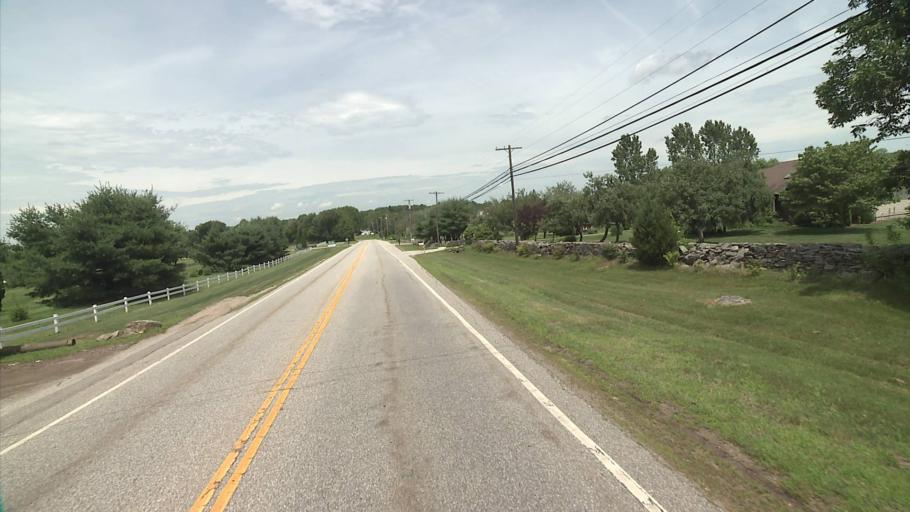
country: US
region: Connecticut
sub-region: New London County
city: Jewett City
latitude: 41.5783
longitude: -71.9772
